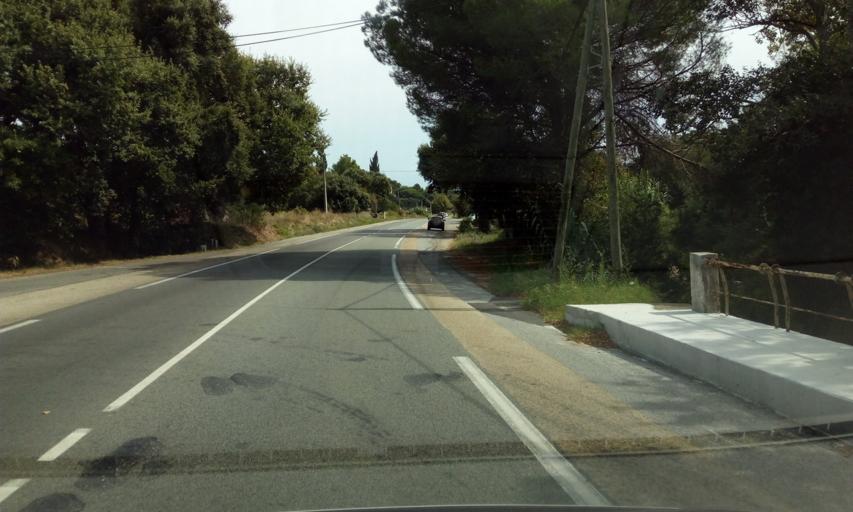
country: FR
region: Provence-Alpes-Cote d'Azur
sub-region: Departement du Var
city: Bormes-les-Mimosas
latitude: 43.1512
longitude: 6.3151
